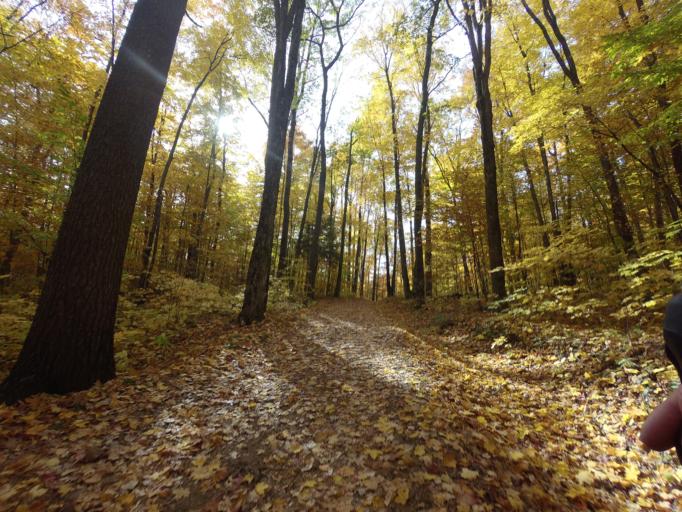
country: CA
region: Quebec
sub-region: Outaouais
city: Gatineau
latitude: 45.5008
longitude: -75.8306
